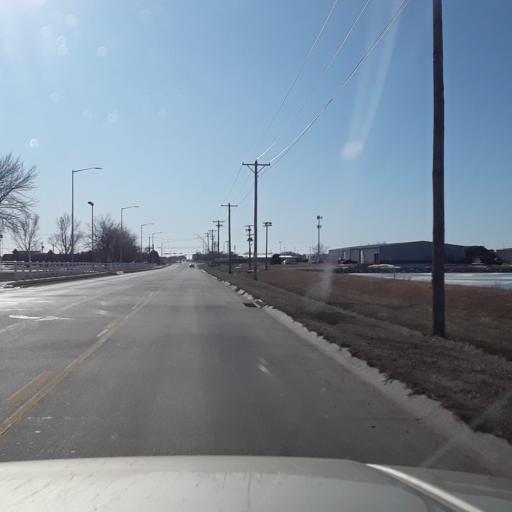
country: US
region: Nebraska
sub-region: Adams County
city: Hastings
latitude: 40.5721
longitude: -98.4021
